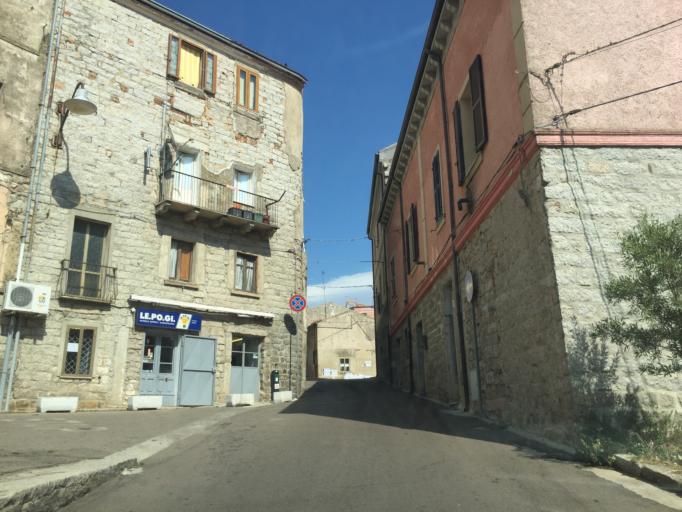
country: IT
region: Sardinia
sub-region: Provincia di Olbia-Tempio
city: Tempio Pausania
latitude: 40.9040
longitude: 9.1020
